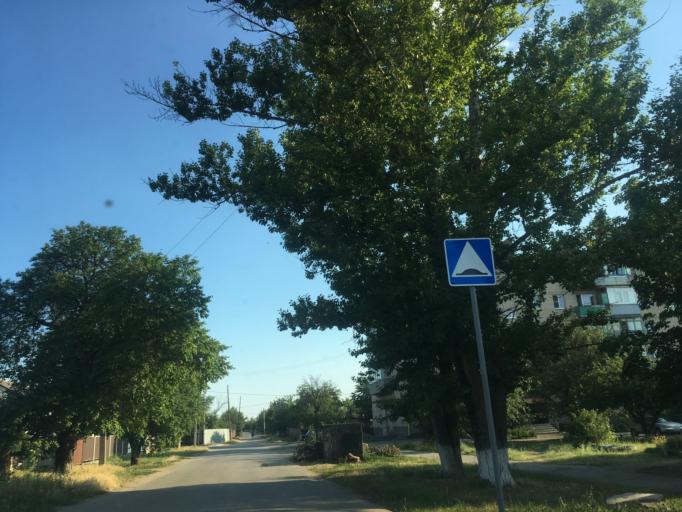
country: RU
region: Rostov
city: Masalovka
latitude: 48.4015
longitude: 40.2773
